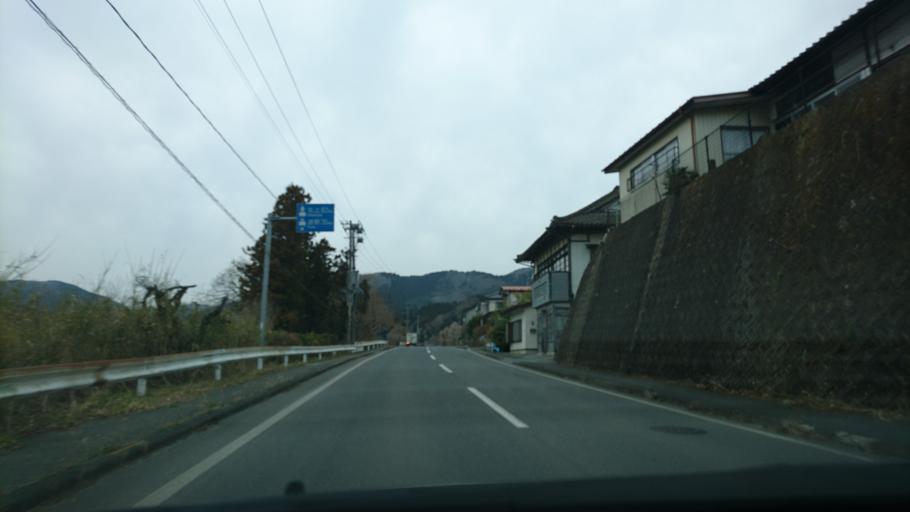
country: JP
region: Iwate
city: Ofunato
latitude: 39.1463
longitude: 141.5756
